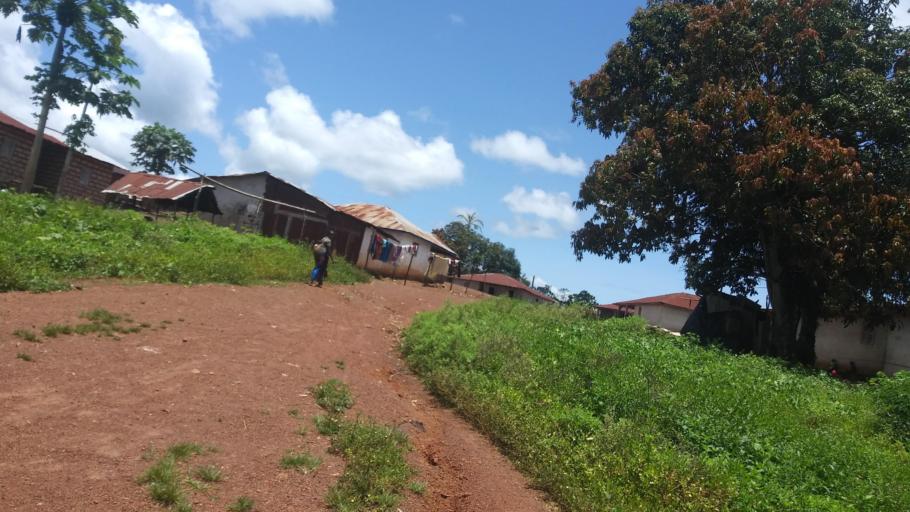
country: SL
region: Northern Province
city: Binkolo
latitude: 8.9010
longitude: -11.9901
